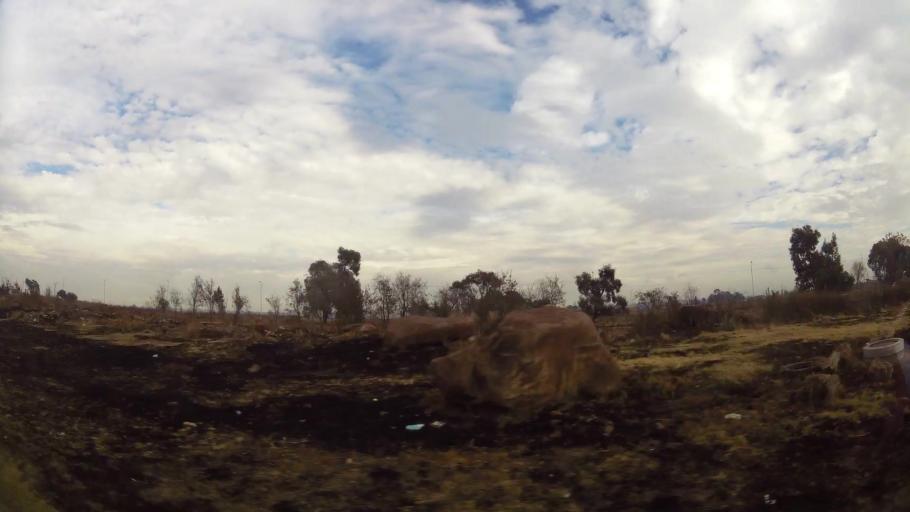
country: ZA
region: Gauteng
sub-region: Ekurhuleni Metropolitan Municipality
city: Germiston
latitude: -26.3320
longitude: 28.1875
